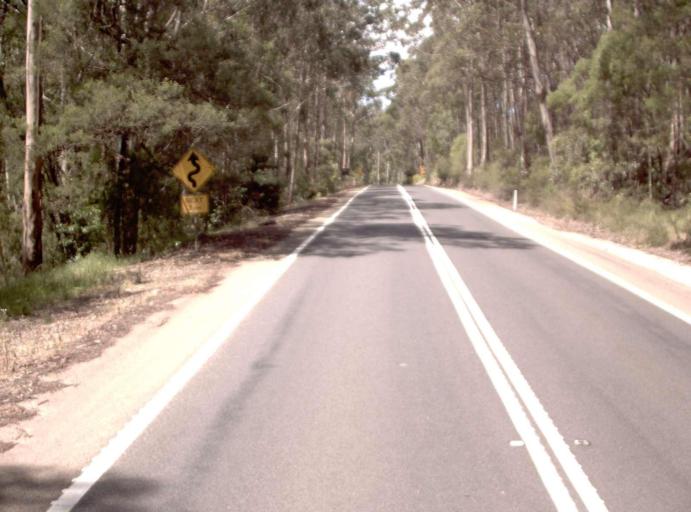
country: AU
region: New South Wales
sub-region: Bombala
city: Bombala
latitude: -37.5639
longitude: 149.3457
